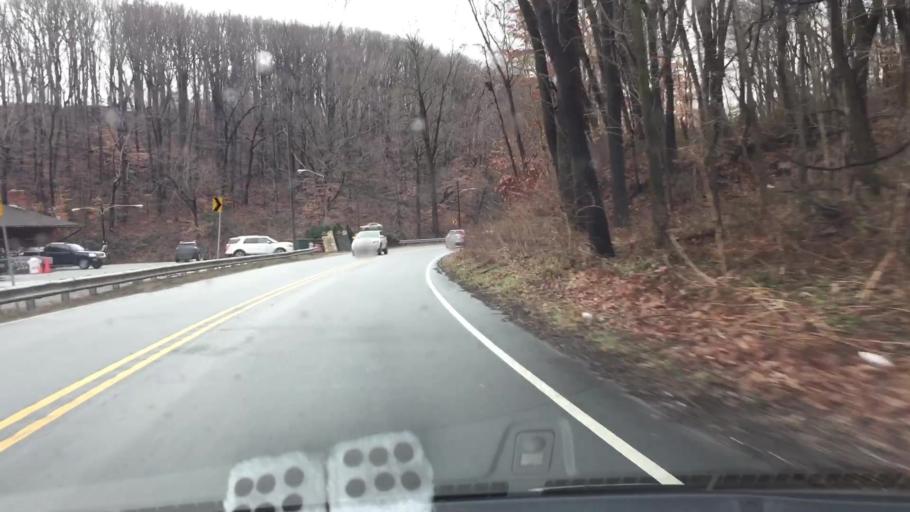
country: US
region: Pennsylvania
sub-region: Delaware County
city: Village Green-Green Ridge
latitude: 39.8821
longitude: -75.4291
